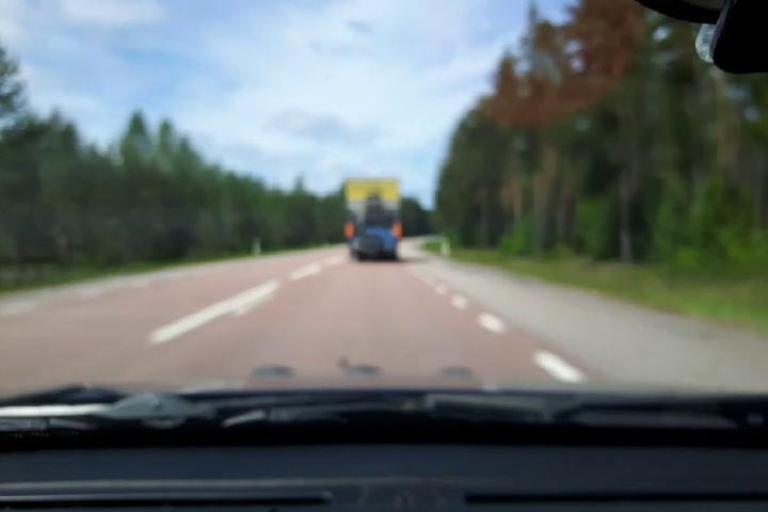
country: SE
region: Uppsala
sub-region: Osthammars Kommun
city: Bjorklinge
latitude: 60.1798
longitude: 17.4807
